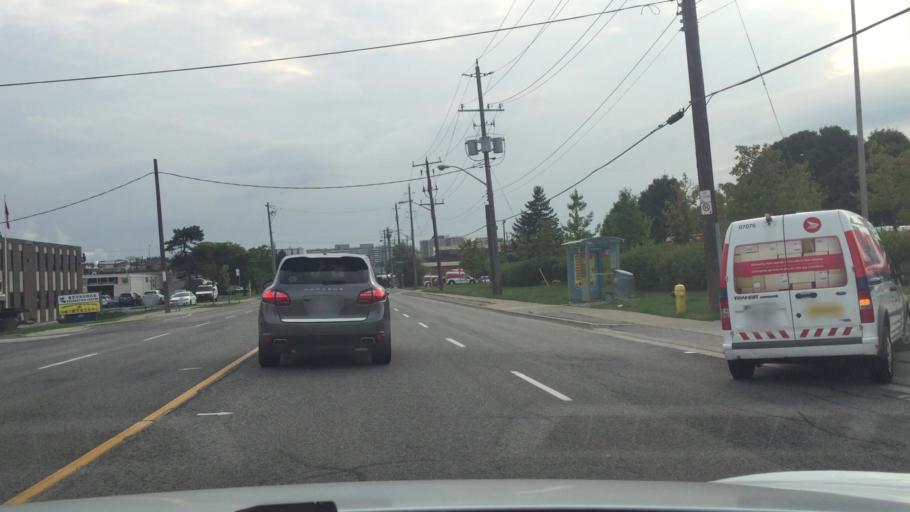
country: CA
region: Ontario
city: Scarborough
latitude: 43.7737
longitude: -79.2697
